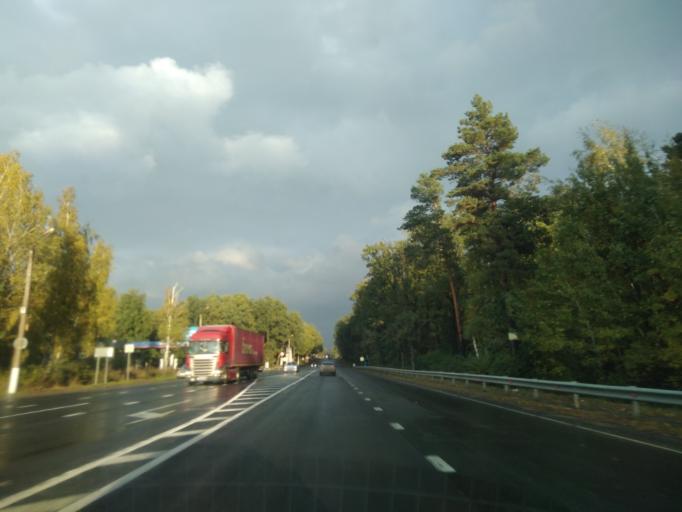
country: RU
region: Lipetsk
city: Donskoye
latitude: 52.5796
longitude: 38.9535
